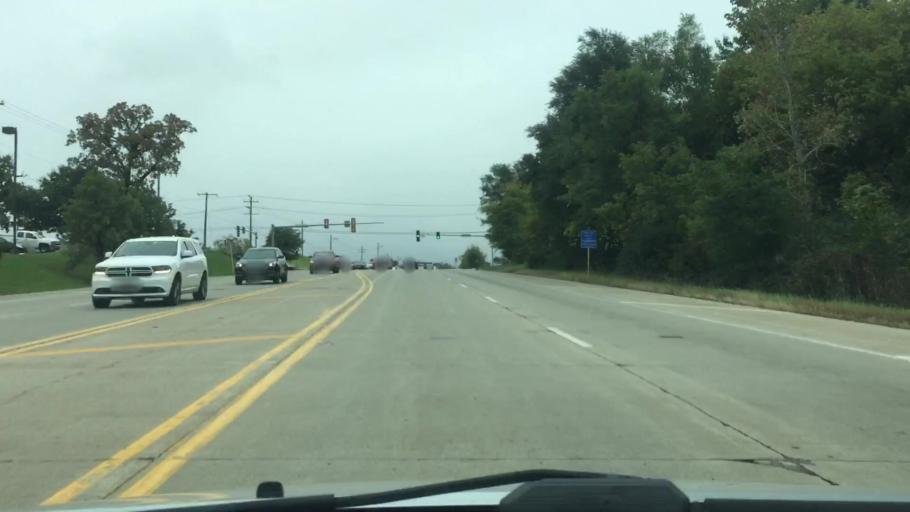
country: US
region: Illinois
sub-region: McHenry County
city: Crystal Lake
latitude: 42.2203
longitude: -88.2868
